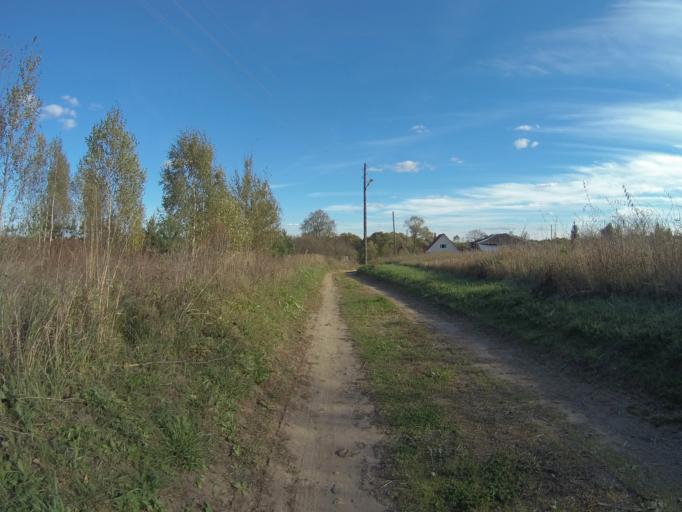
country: RU
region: Vladimir
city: Golovino
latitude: 55.9932
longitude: 40.5268
